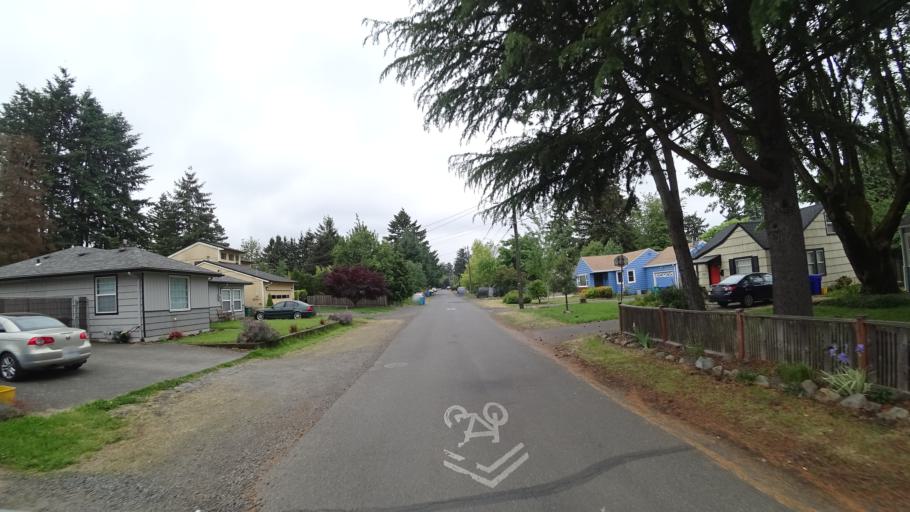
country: US
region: Oregon
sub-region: Multnomah County
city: Portland
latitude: 45.5584
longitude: -122.6114
